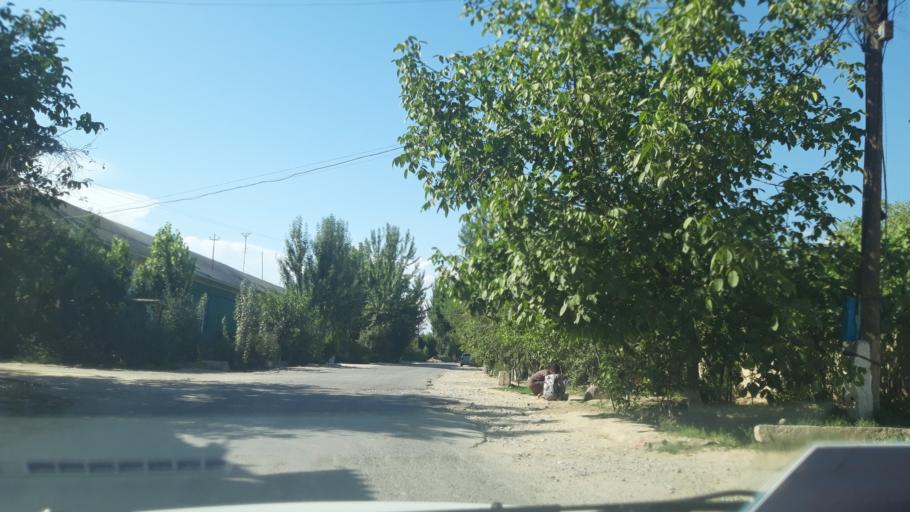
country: UZ
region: Namangan
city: Yangiqo`rg`on
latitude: 41.2059
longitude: 71.7262
